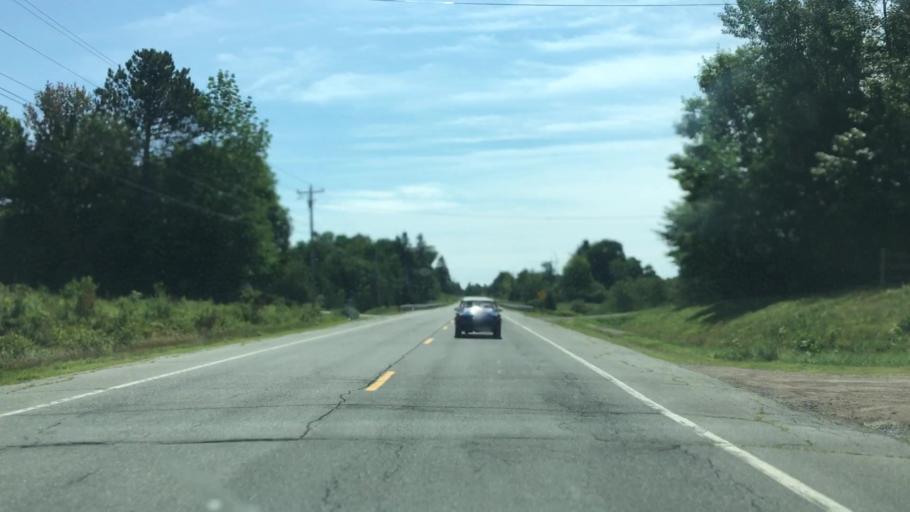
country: CA
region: New Brunswick
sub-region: Charlotte County
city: Saint Andrews
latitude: 45.0953
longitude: -67.1242
